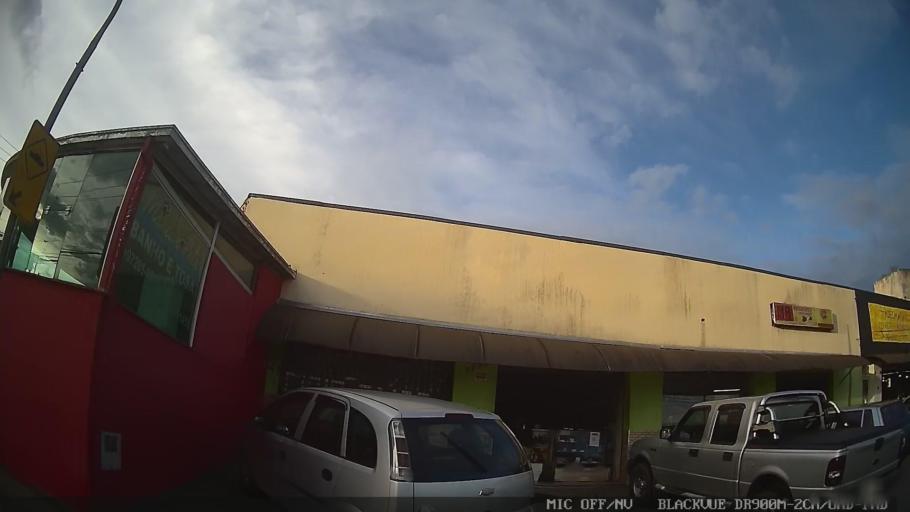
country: BR
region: Sao Paulo
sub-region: Mogi das Cruzes
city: Mogi das Cruzes
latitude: -23.5352
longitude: -46.1711
